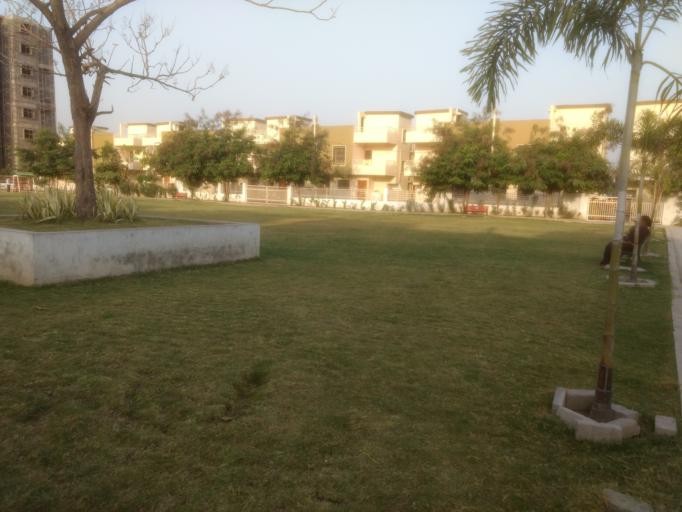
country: IN
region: Maharashtra
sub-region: Nagpur Division
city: Nagpur
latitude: 21.0950
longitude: 79.1477
